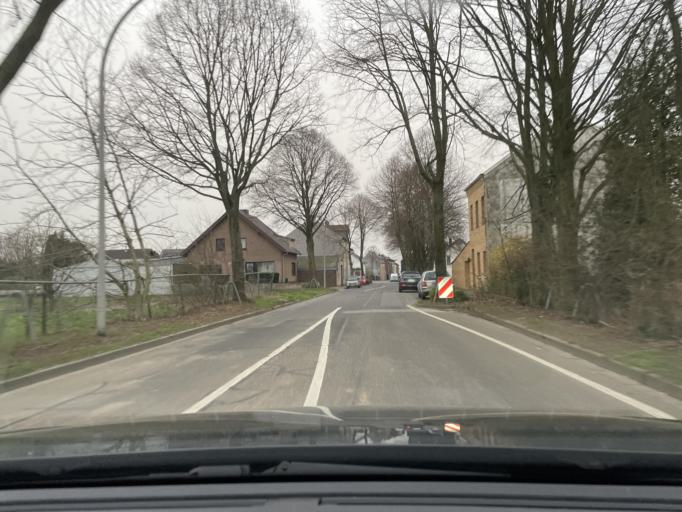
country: DE
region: North Rhine-Westphalia
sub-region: Regierungsbezirk Dusseldorf
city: Juchen
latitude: 51.1024
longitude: 6.4465
